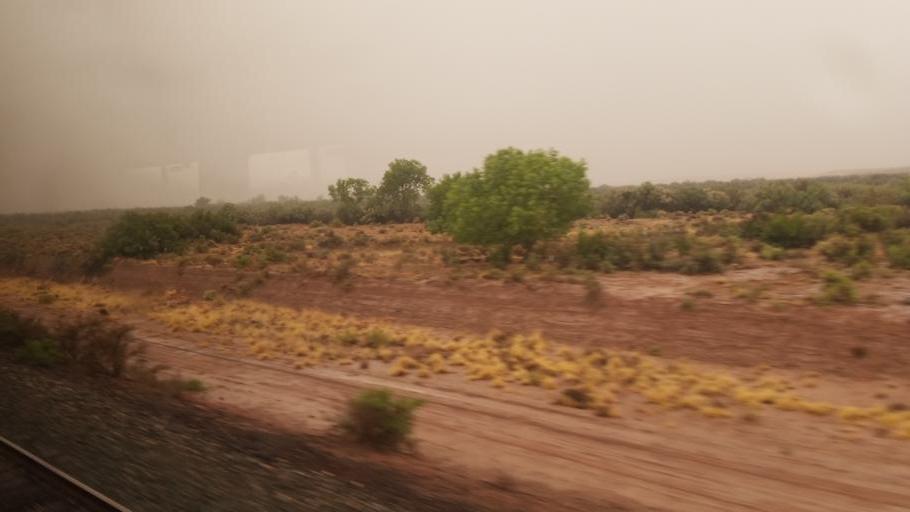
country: US
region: Arizona
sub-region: Navajo County
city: Joseph City
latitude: 34.9534
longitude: -110.3522
